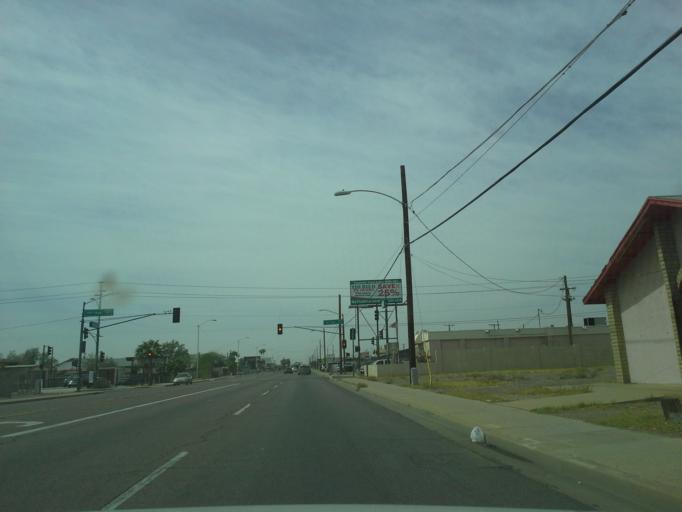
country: US
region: Arizona
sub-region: Maricopa County
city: Phoenix
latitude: 33.4368
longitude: -112.0904
